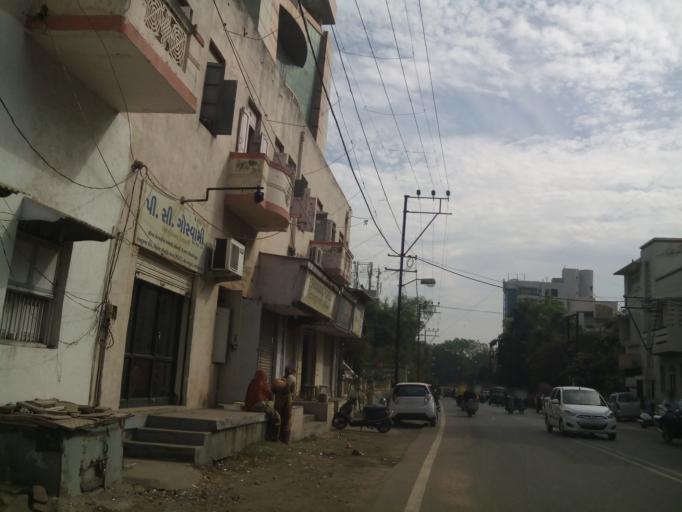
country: IN
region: Gujarat
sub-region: Rajkot
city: Rajkot
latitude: 22.3017
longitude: 70.7991
